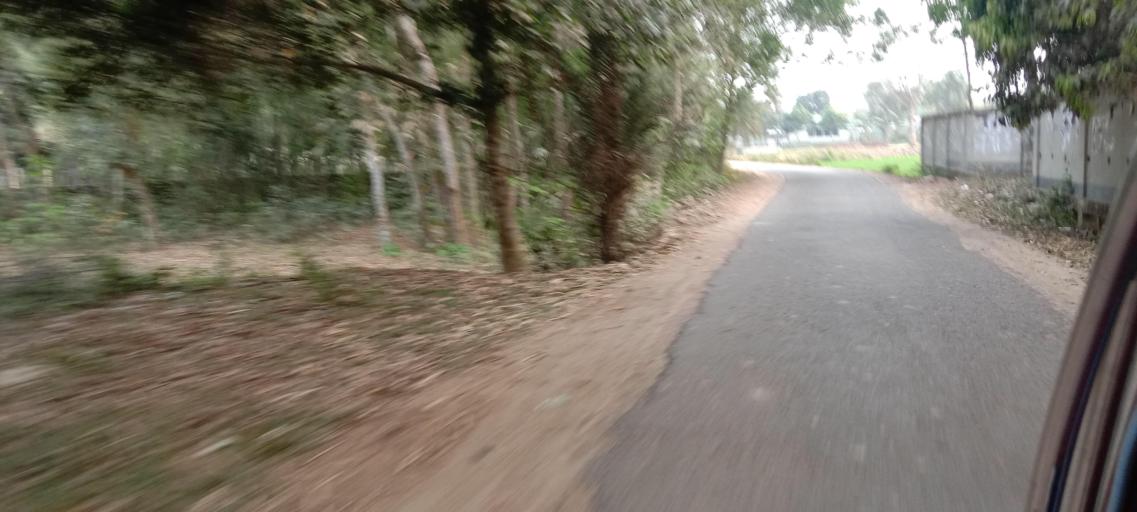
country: BD
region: Dhaka
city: Sakhipur
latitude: 24.4379
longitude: 90.2626
